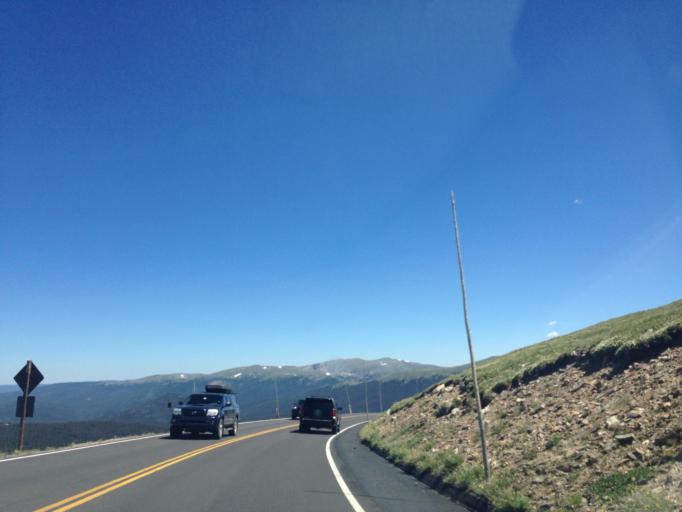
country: US
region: Colorado
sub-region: Larimer County
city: Estes Park
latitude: 40.4340
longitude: -105.7680
